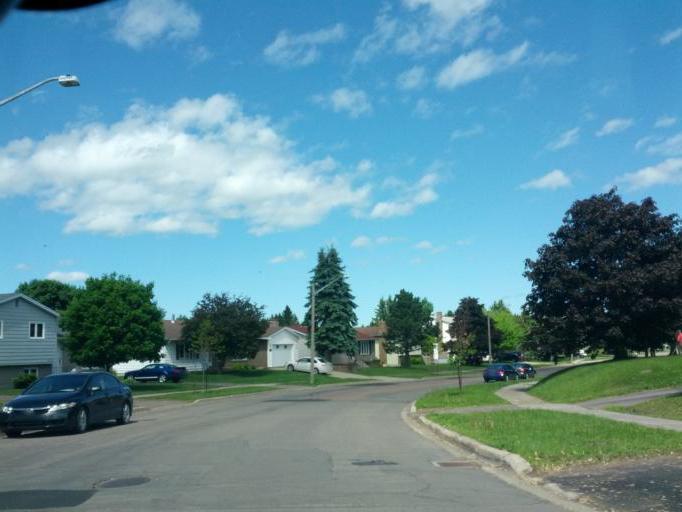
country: CA
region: New Brunswick
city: Moncton
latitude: 46.1251
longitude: -64.8524
